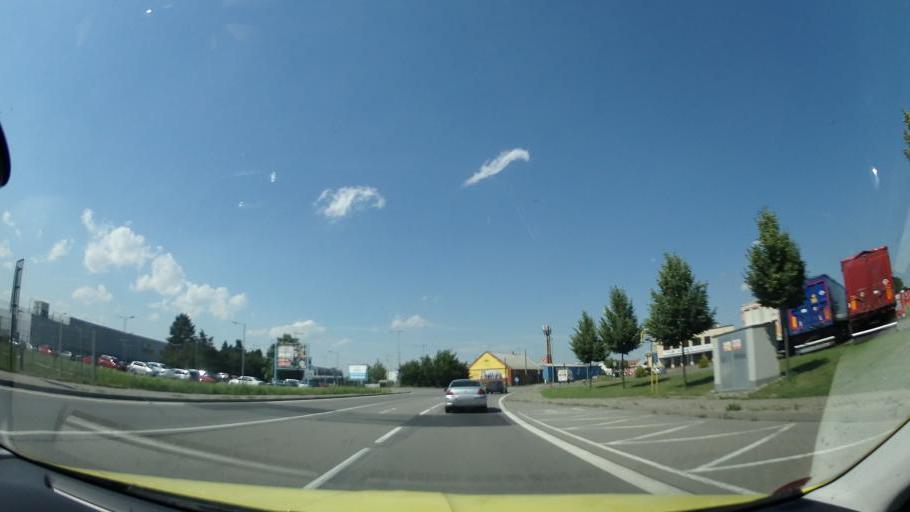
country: CZ
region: Olomoucky
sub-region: Okres Olomouc
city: Olomouc
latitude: 49.5611
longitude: 17.2619
